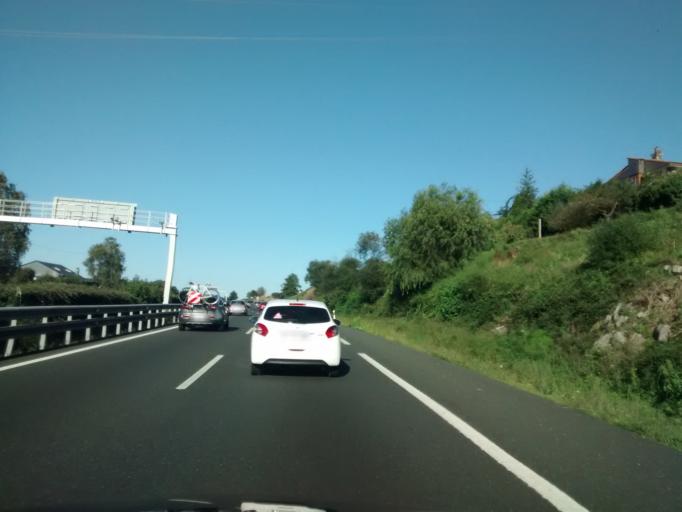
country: ES
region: Cantabria
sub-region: Provincia de Cantabria
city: Santa Cruz de Bezana
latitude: 43.4263
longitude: -3.9335
